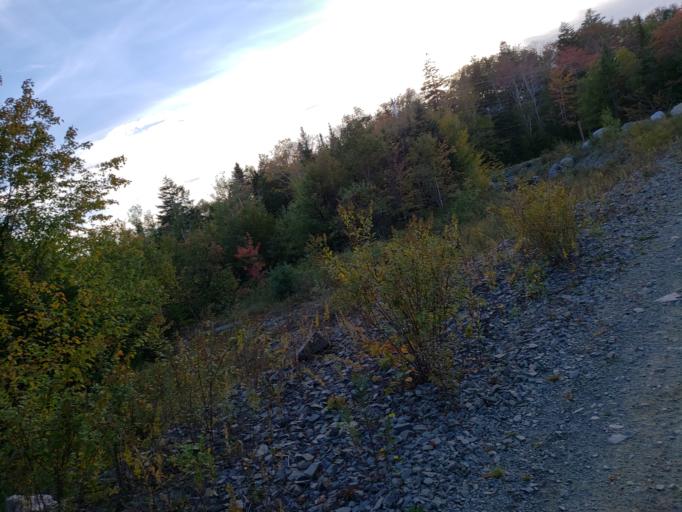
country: CA
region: Nova Scotia
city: Cole Harbour
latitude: 44.7435
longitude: -63.3782
